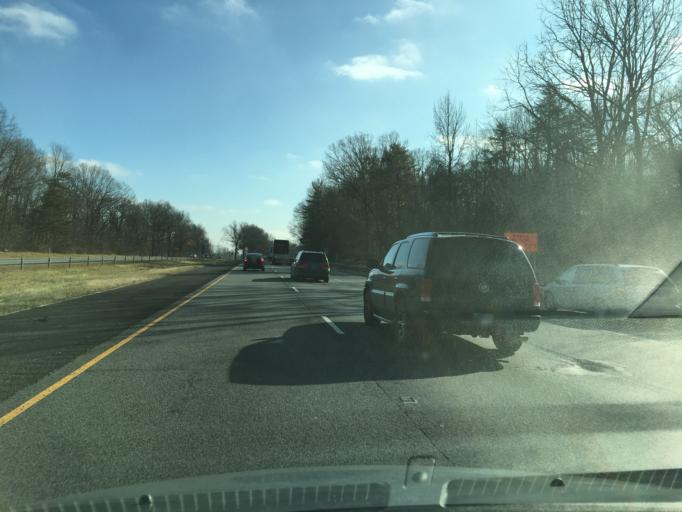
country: US
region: Indiana
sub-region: Marion County
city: Clermont
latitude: 39.8763
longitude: -86.2881
